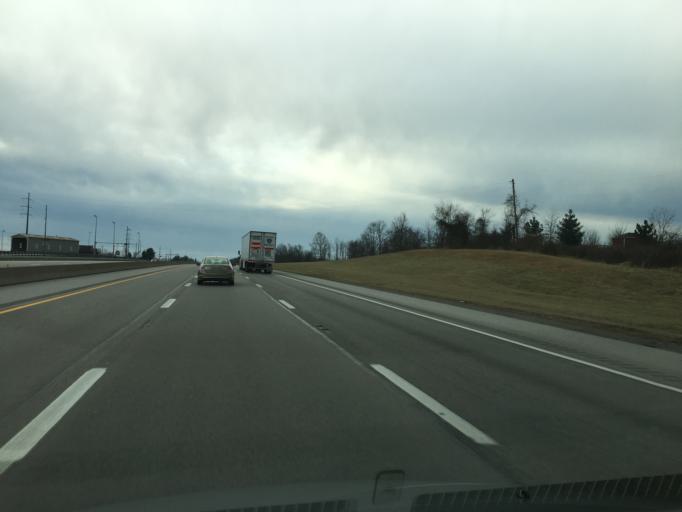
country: US
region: Kentucky
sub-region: Scott County
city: Georgetown
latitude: 38.2959
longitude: -84.5589
